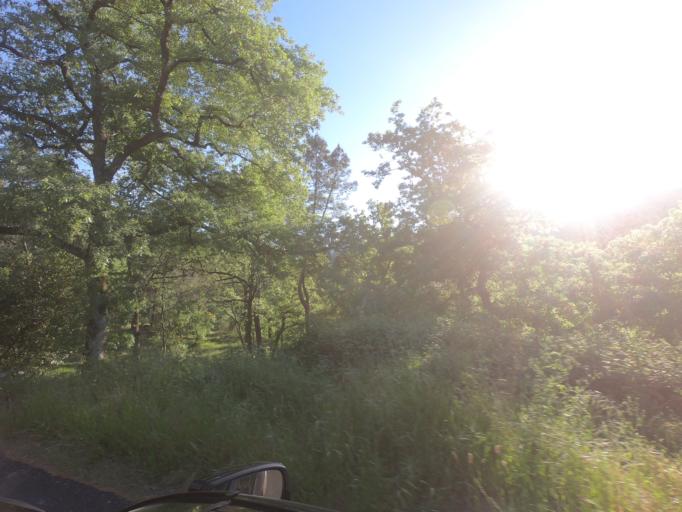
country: PT
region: Vila Real
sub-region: Vila Real
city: Vila Real
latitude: 41.3364
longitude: -7.7335
